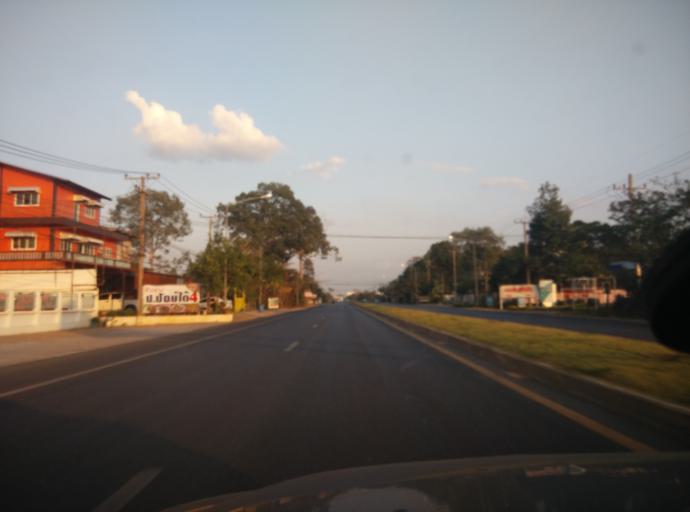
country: TH
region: Sisaket
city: Si Sa Ket
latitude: 15.1255
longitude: 104.2894
